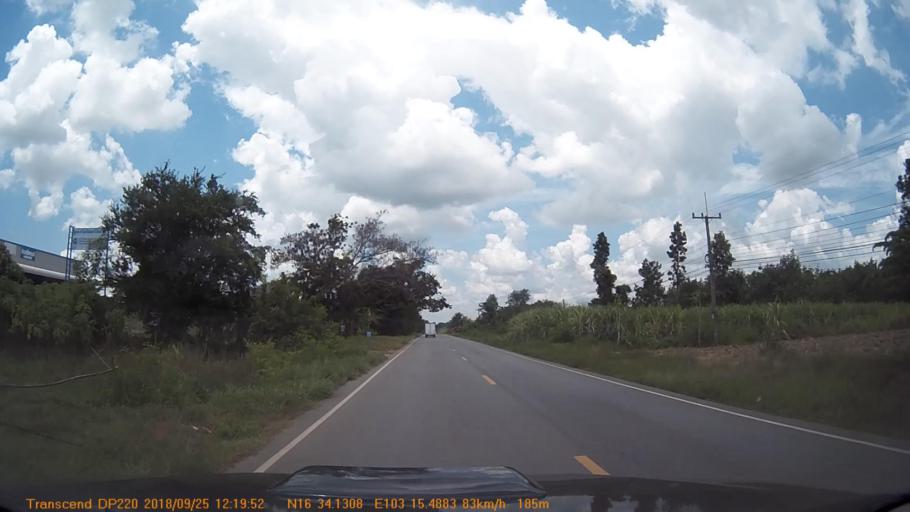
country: TH
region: Kalasin
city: Huai Mek
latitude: 16.5689
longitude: 103.2580
